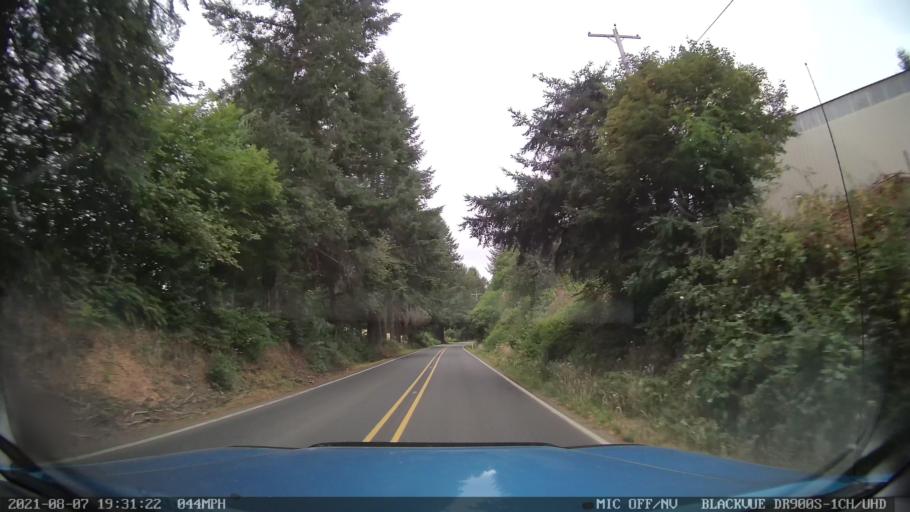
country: US
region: Oregon
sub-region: Linn County
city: Lyons
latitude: 44.8911
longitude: -122.6326
